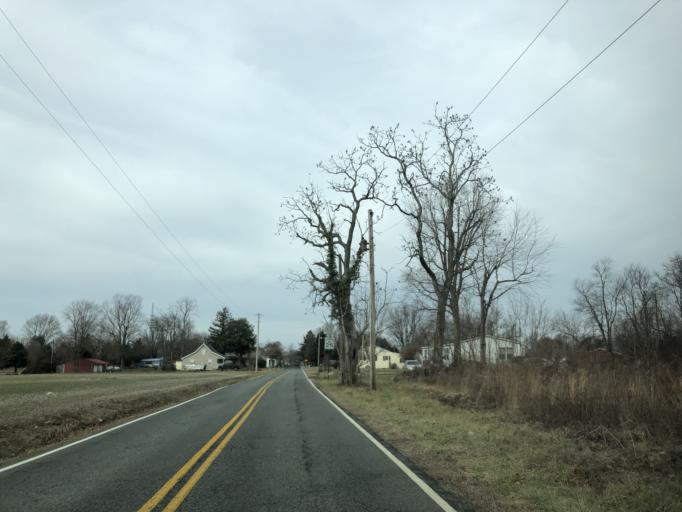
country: US
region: Delaware
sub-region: New Castle County
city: Middletown
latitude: 39.4174
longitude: -75.7718
